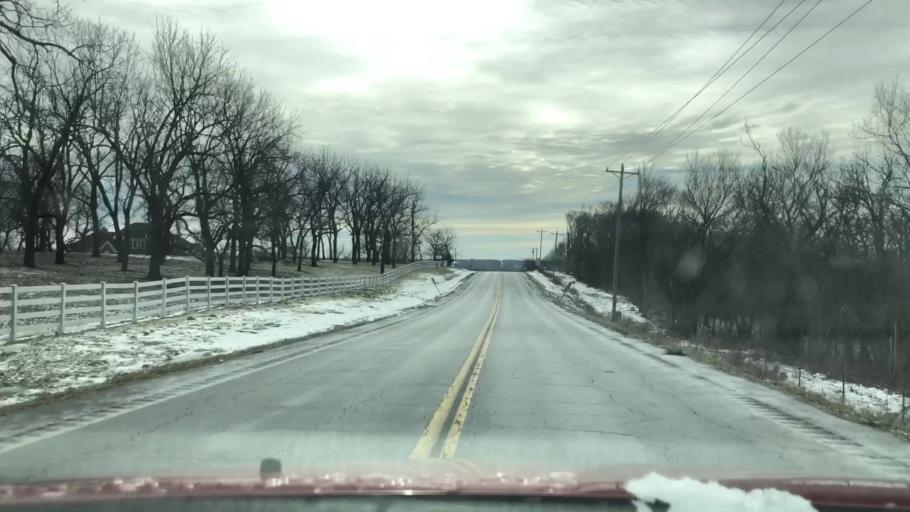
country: US
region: Missouri
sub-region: Jackson County
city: Oak Grove
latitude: 38.9323
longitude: -94.1325
